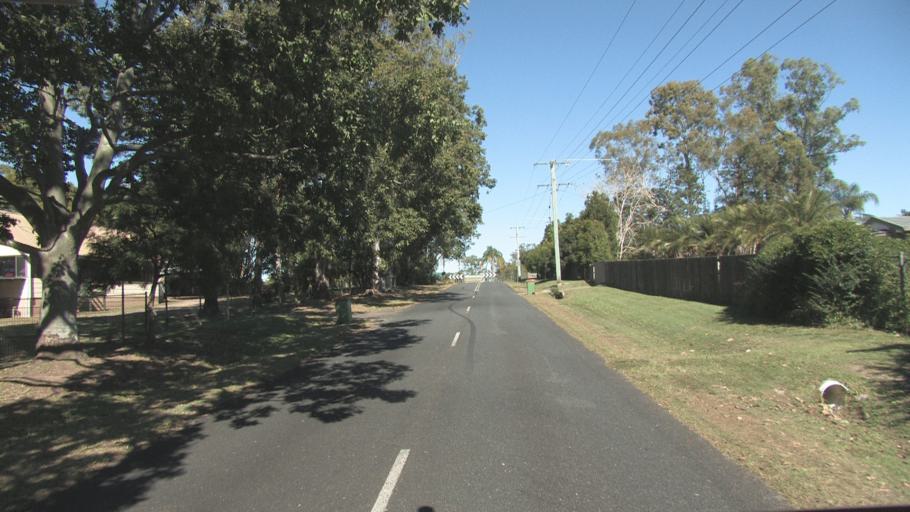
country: AU
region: Queensland
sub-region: Logan
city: Park Ridge South
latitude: -27.7178
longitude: 153.0575
